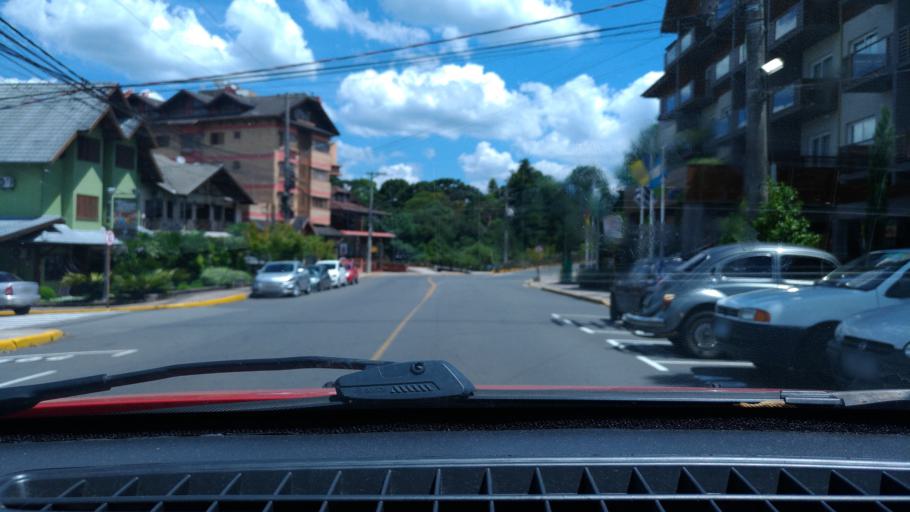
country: BR
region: Rio Grande do Sul
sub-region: Canela
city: Canela
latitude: -29.3843
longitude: -50.8720
